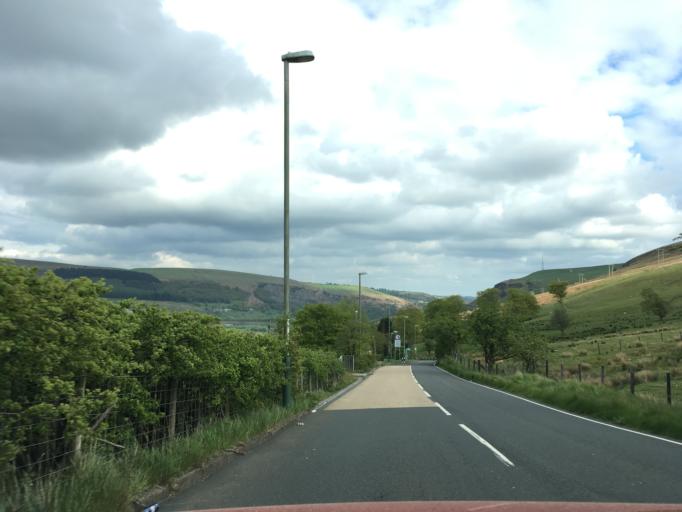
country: GB
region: Wales
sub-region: Caerphilly County Borough
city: Rhymney
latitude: 51.7444
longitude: -3.2856
